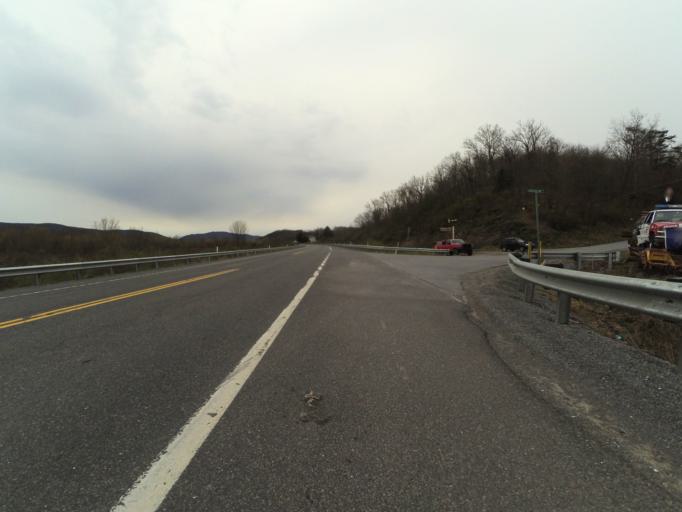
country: US
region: Pennsylvania
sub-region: Centre County
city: Milesburg
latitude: 40.9755
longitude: -77.7452
